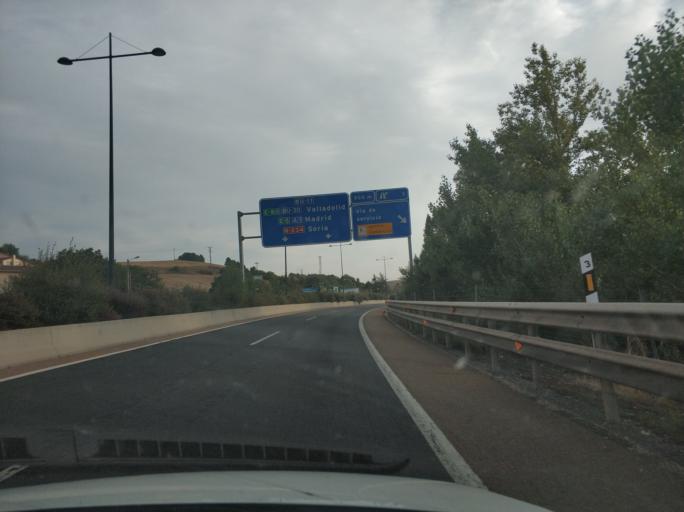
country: ES
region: Castille and Leon
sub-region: Provincia de Burgos
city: Burgos
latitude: 42.3289
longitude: -3.6964
